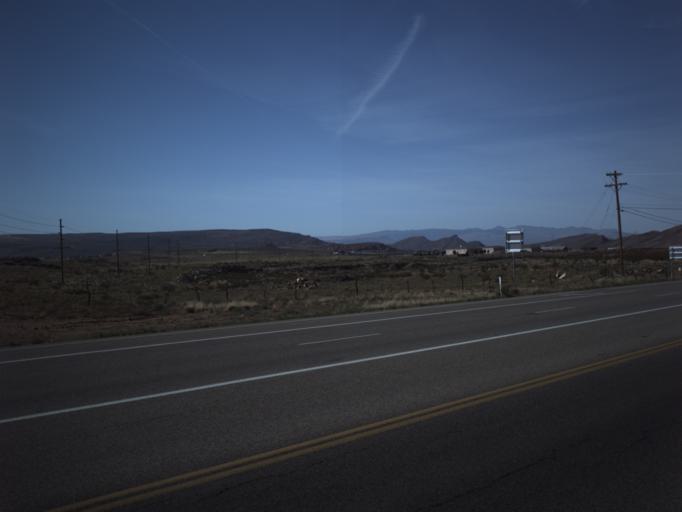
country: US
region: Utah
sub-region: Washington County
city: Hurricane
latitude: 37.1673
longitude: -113.3750
